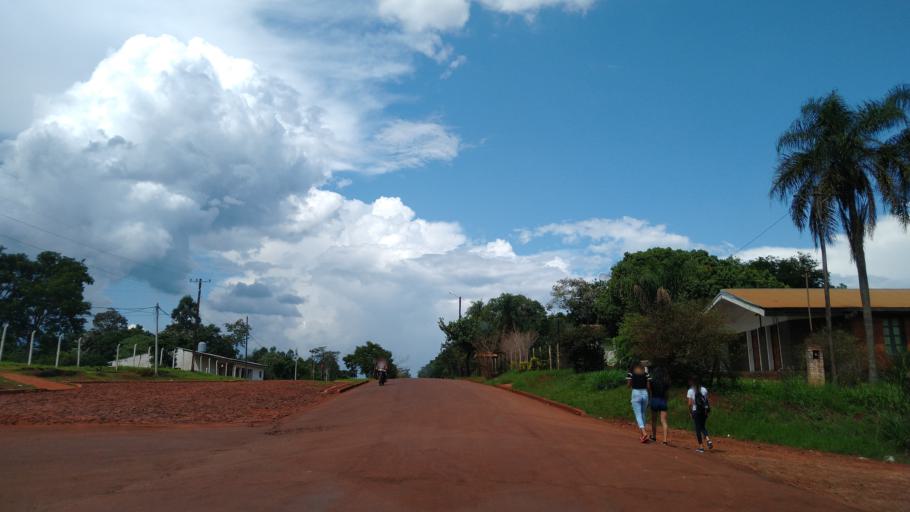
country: AR
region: Misiones
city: Puerto Libertad
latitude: -25.9666
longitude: -54.5935
